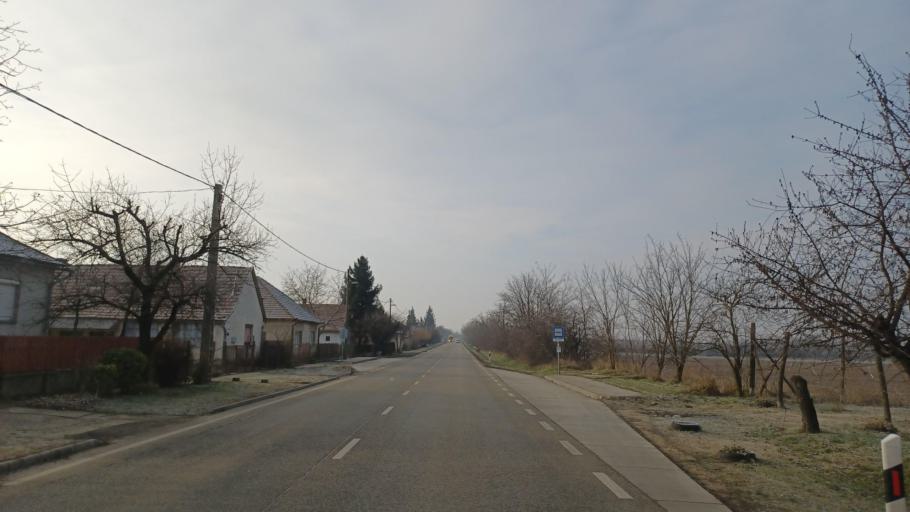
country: HU
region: Tolna
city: Simontornya
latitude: 46.7451
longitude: 18.5242
